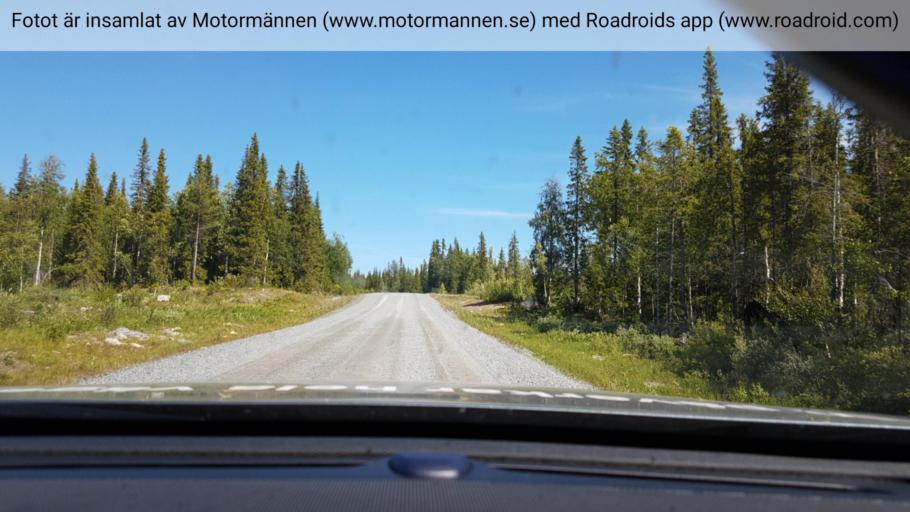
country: SE
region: Vaesterbotten
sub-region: Vilhelmina Kommun
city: Sjoberg
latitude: 64.7172
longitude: 15.7780
